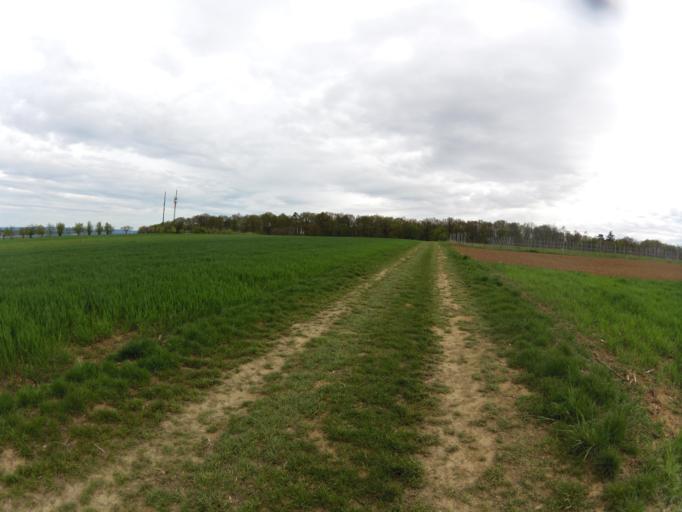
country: DE
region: Bavaria
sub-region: Regierungsbezirk Unterfranken
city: Nordheim
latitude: 49.8598
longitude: 10.1603
